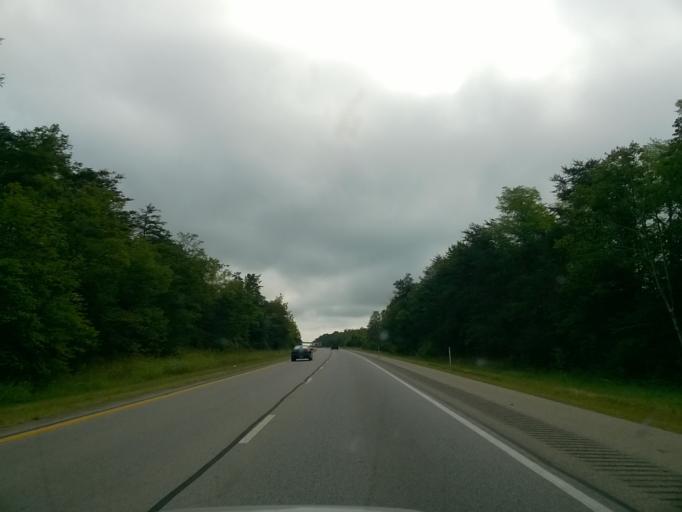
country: US
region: Indiana
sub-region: Floyd County
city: Georgetown
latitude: 38.2757
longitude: -85.9579
